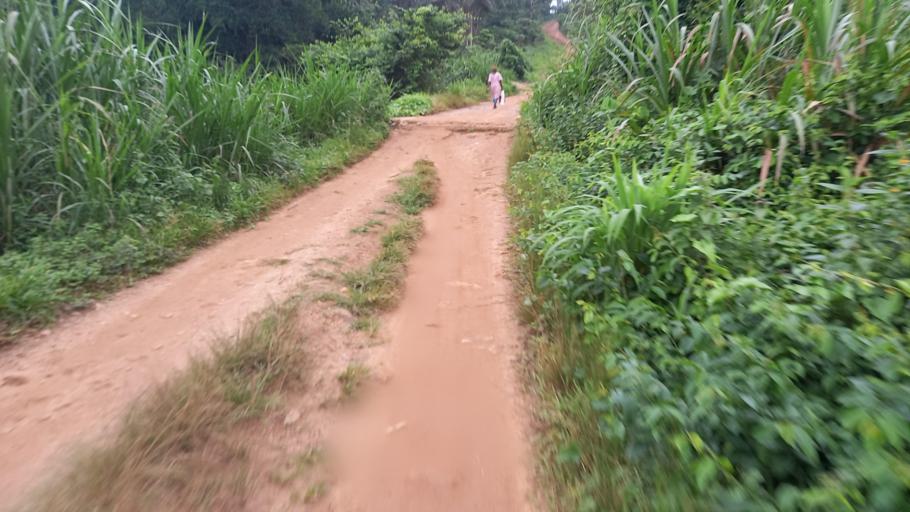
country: SL
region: Eastern Province
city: Kailahun
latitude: 8.2378
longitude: -10.5180
